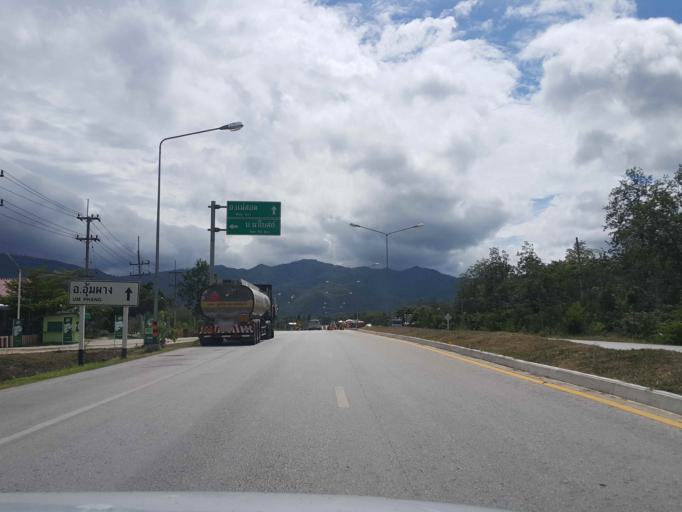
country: TH
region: Tak
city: Tak
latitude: 16.8042
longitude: 99.0448
